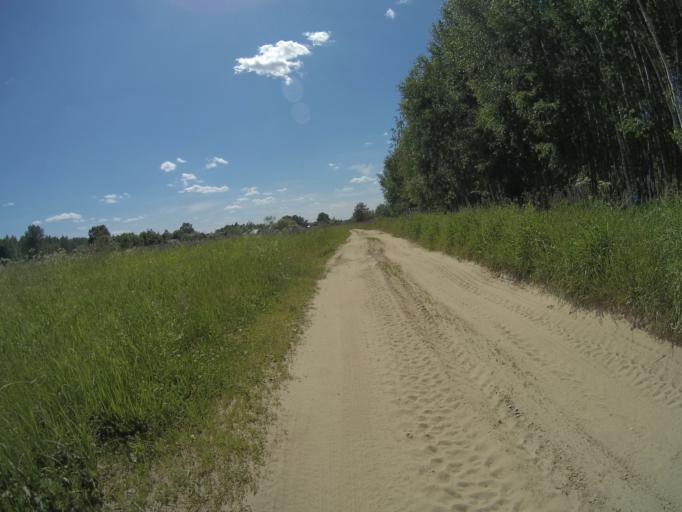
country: RU
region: Vladimir
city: Golovino
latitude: 56.0064
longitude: 40.4441
